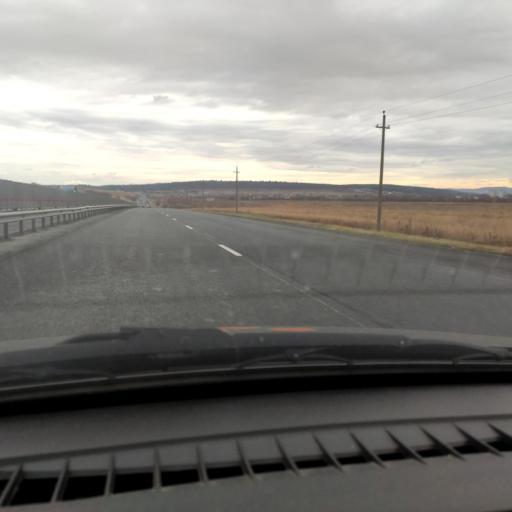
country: RU
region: Samara
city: Kurumoch
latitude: 53.5014
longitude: 50.0110
